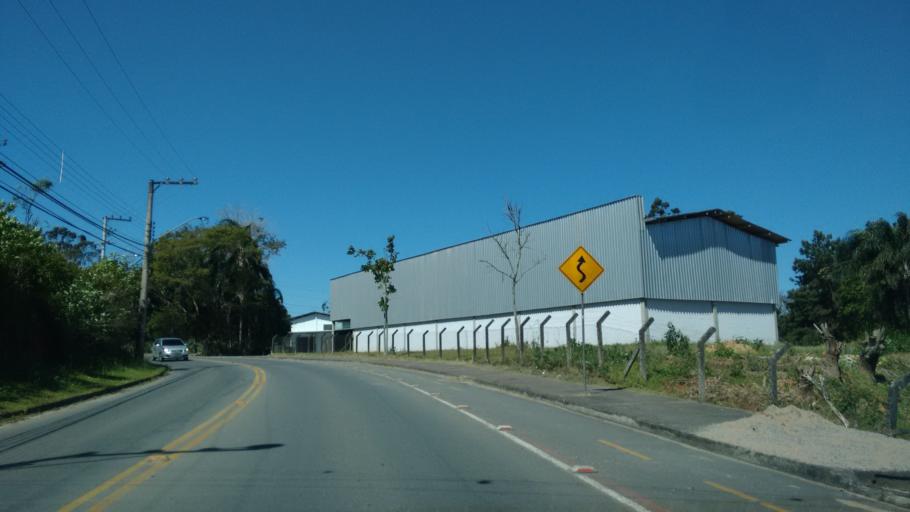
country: BR
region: Santa Catarina
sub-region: Blumenau
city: Blumenau
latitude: -26.8884
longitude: -49.1270
